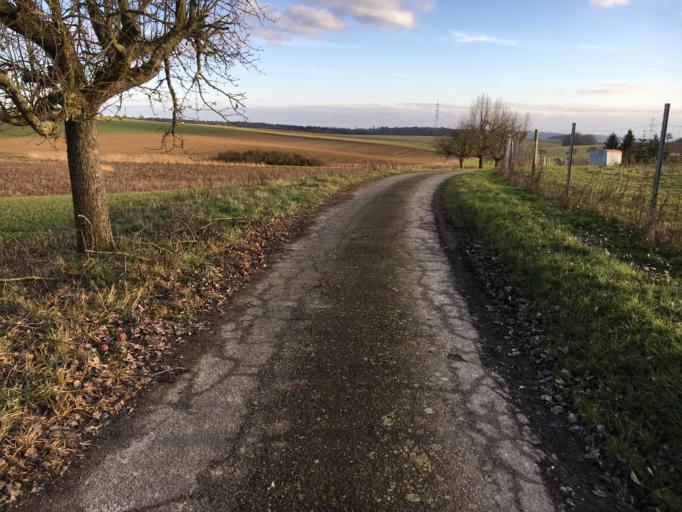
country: DE
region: Baden-Wuerttemberg
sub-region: Karlsruhe Region
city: Billigheim
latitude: 49.3727
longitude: 9.2055
